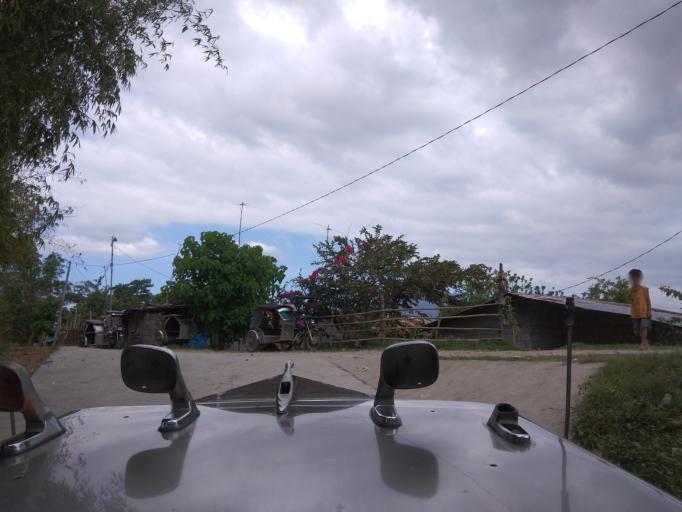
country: PH
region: Central Luzon
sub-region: Province of Pampanga
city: San Patricio
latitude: 15.1121
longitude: 120.7187
